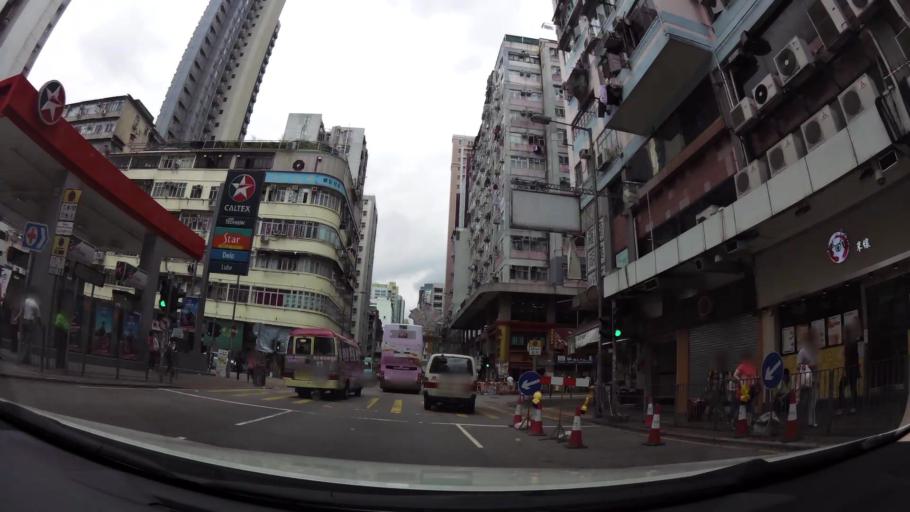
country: HK
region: Sham Shui Po
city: Sham Shui Po
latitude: 22.3350
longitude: 114.1596
